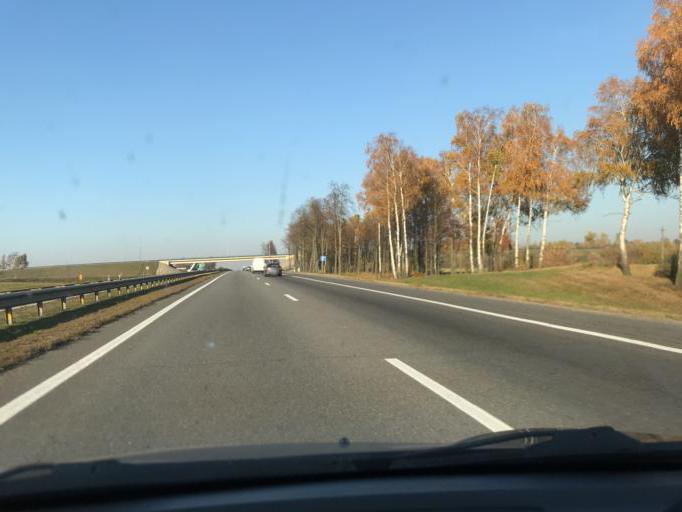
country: BY
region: Minsk
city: Yubilyeyny
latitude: 53.7849
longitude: 27.5264
